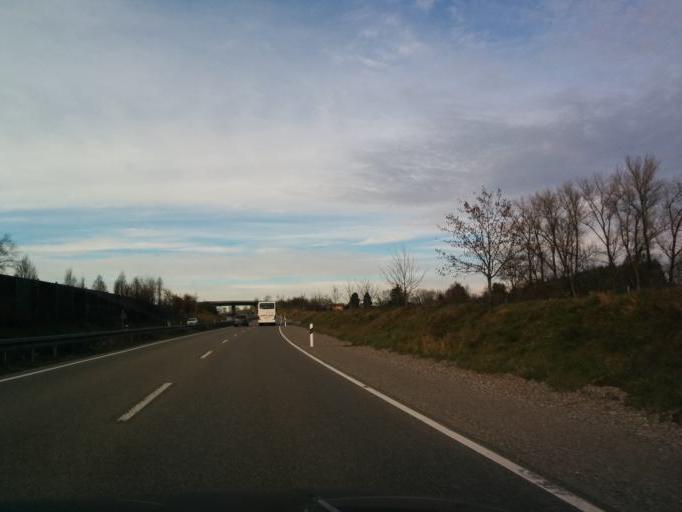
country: DE
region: Bavaria
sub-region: Swabia
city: Waltenhofen
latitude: 47.6616
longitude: 10.2988
